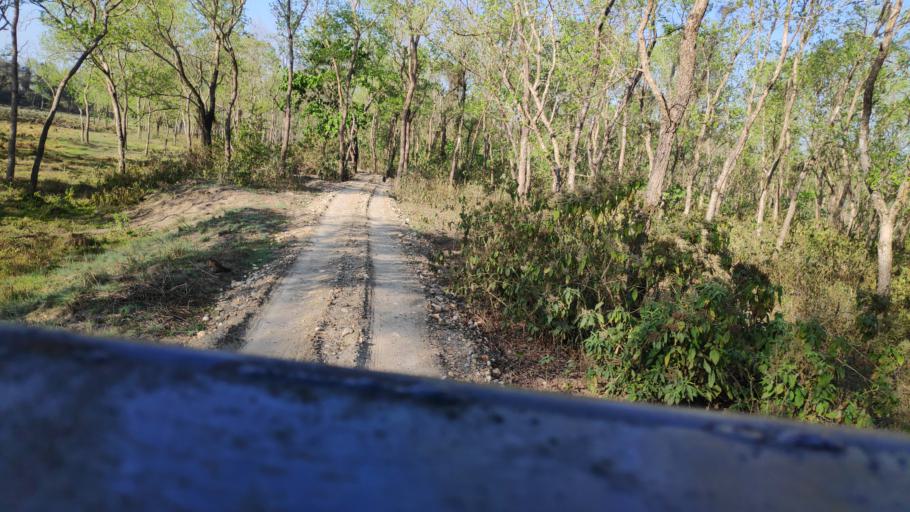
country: NP
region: Central Region
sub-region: Narayani Zone
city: Bharatpur
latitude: 27.5615
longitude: 84.5708
